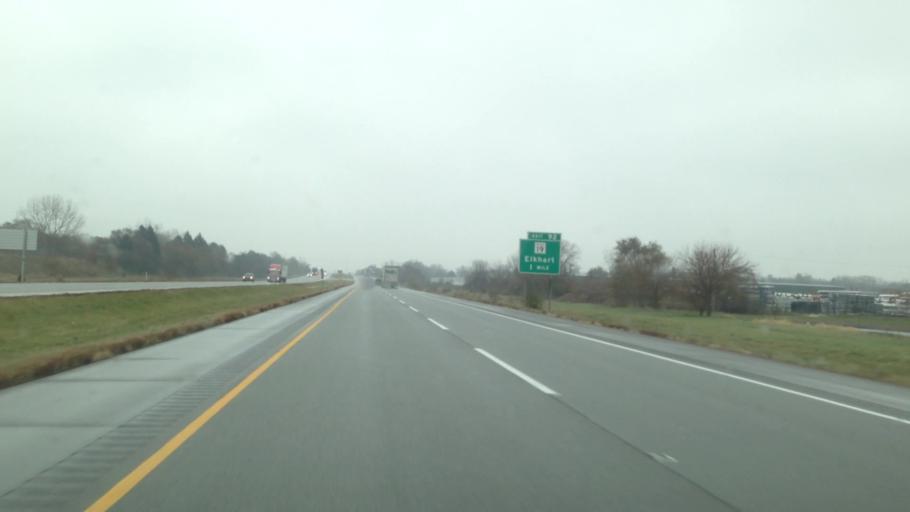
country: US
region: Indiana
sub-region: Elkhart County
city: Simonton Lake
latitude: 41.7319
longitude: -85.9961
